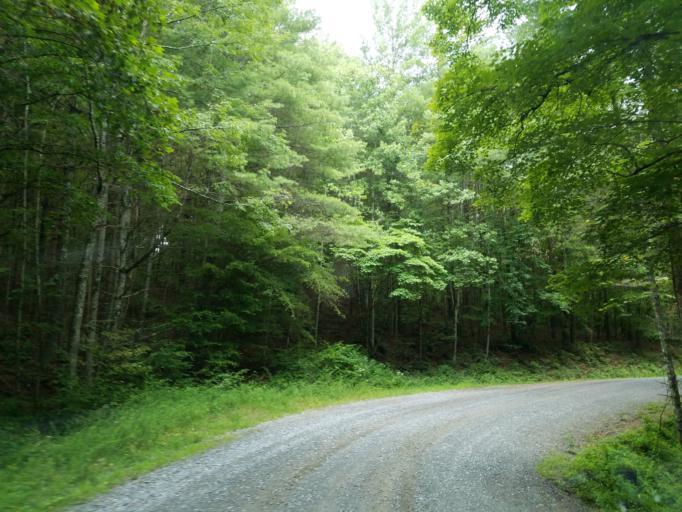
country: US
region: Georgia
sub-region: Fannin County
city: Blue Ridge
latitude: 34.8177
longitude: -84.2401
